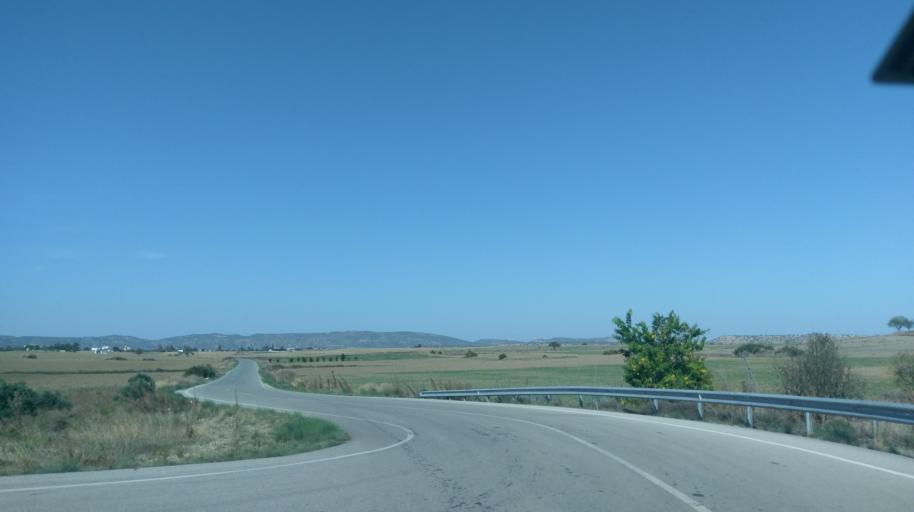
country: CY
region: Ammochostos
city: Leonarisso
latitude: 35.3804
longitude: 34.0215
